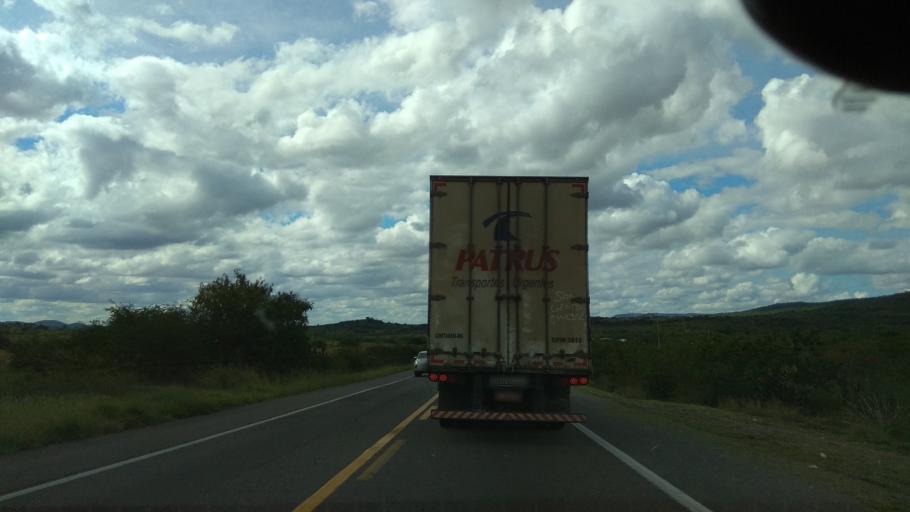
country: BR
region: Bahia
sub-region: Santa Ines
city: Santa Ines
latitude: -12.9894
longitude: -39.9462
